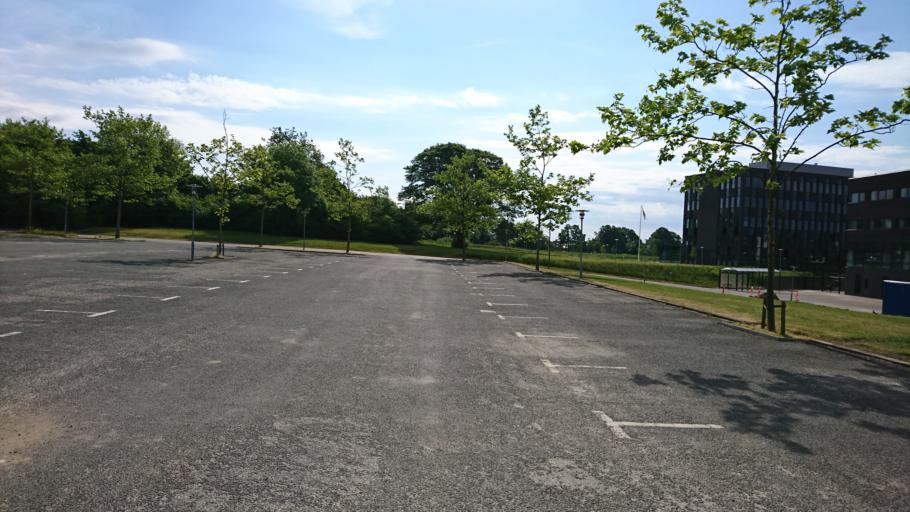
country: DK
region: Capital Region
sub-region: Ballerup Kommune
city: Ballerup
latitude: 55.7295
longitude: 12.3924
